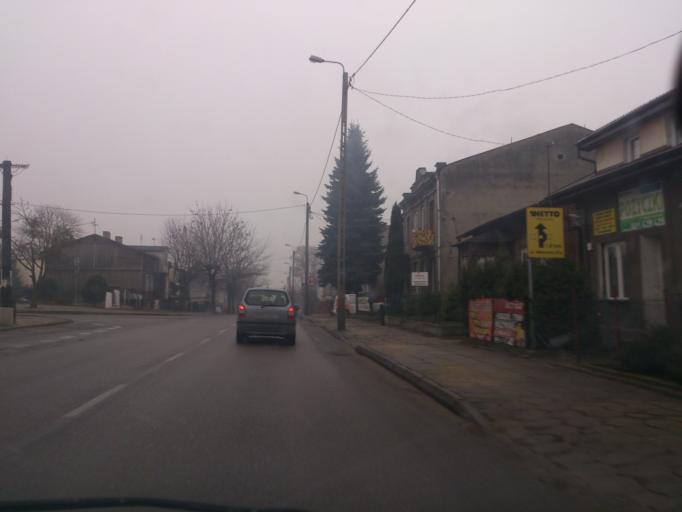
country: PL
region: Kujawsko-Pomorskie
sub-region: Powiat rypinski
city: Rypin
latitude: 53.0722
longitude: 19.4007
